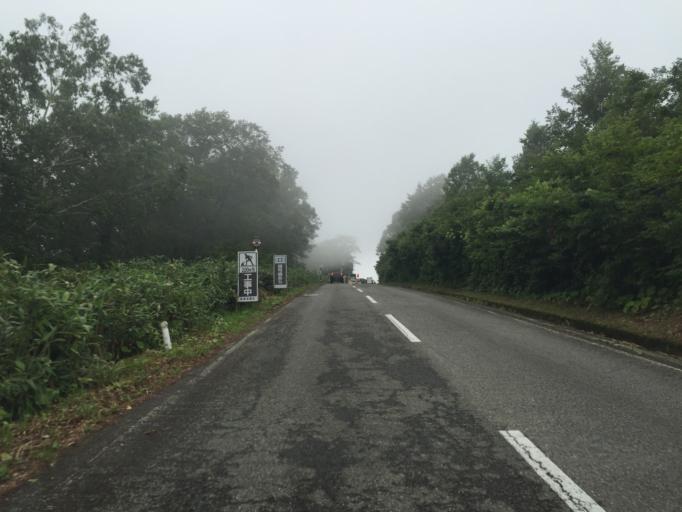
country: JP
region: Yamagata
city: Yonezawa
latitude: 37.7516
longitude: 140.0904
